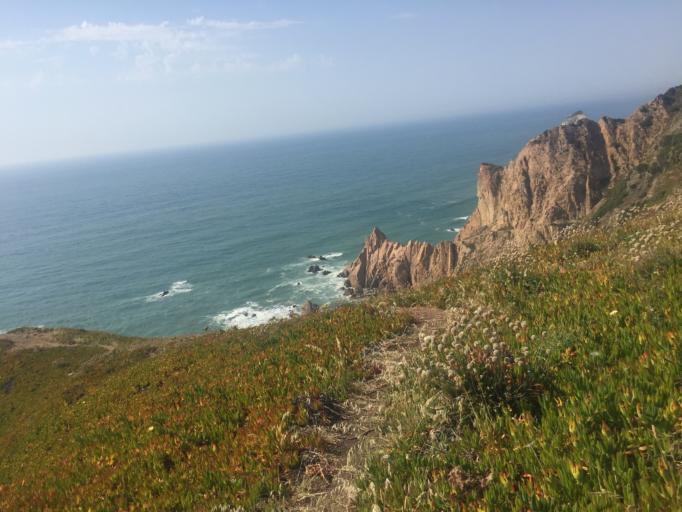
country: PT
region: Lisbon
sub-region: Sintra
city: Colares
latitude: 38.7844
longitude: -9.4956
